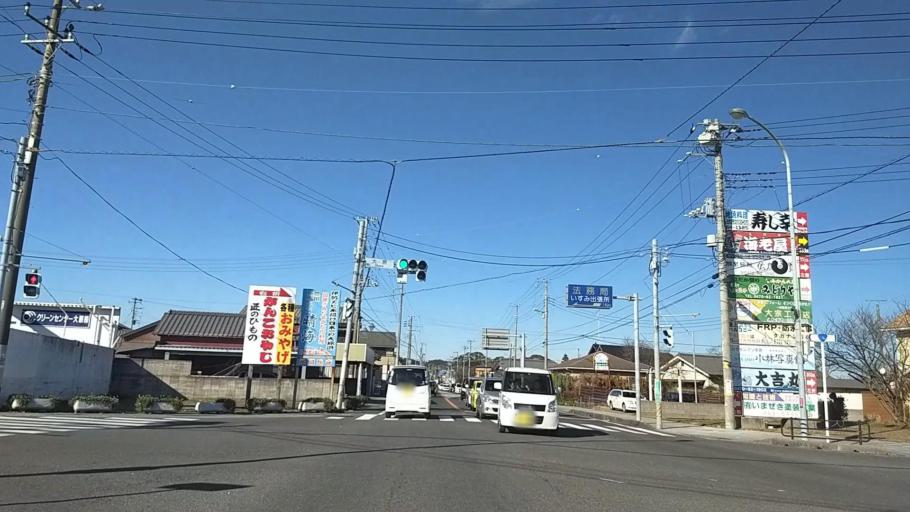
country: JP
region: Chiba
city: Ohara
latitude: 35.2539
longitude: 140.3954
